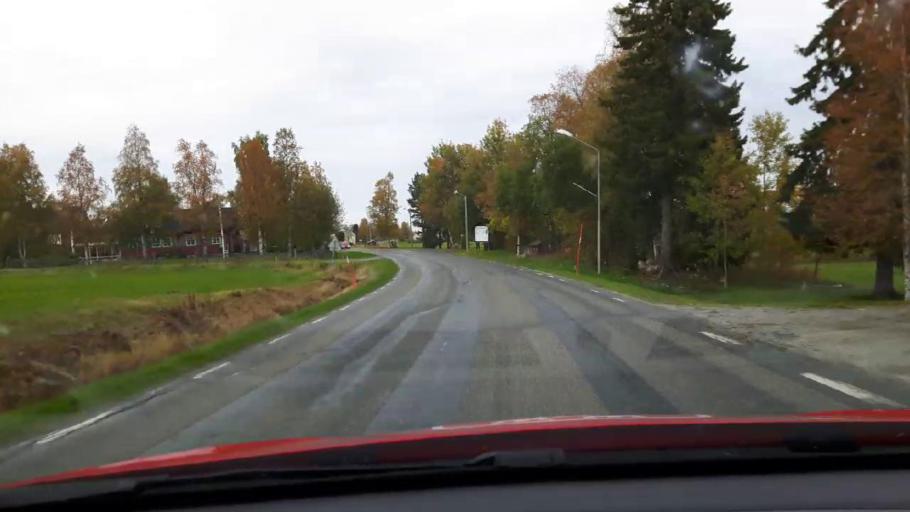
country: SE
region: Jaemtland
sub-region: Bergs Kommun
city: Hoverberg
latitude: 62.8423
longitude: 14.3843
